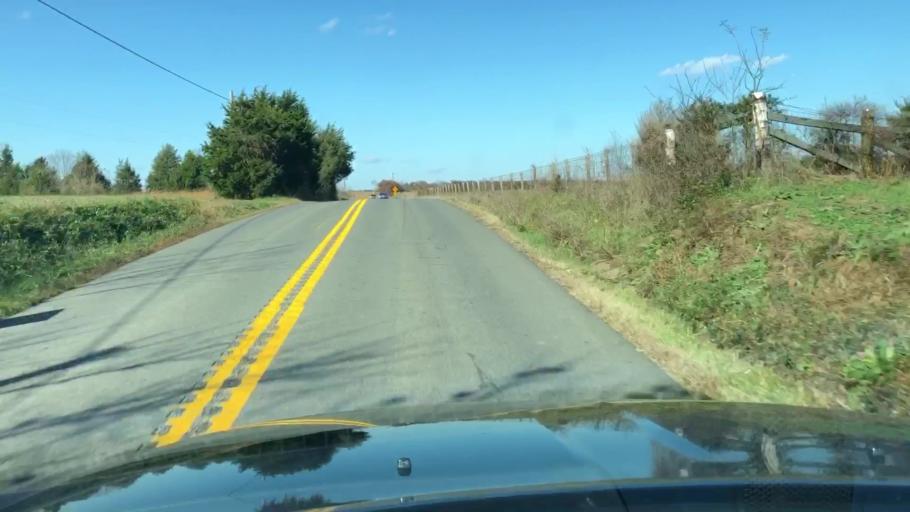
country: US
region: Virginia
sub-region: Fauquier County
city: Bealeton
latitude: 38.5093
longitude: -77.7779
